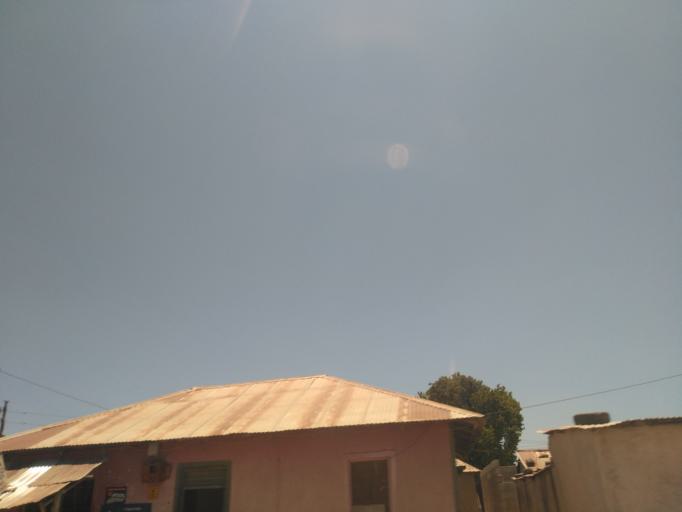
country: TZ
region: Dodoma
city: Dodoma
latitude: -6.1626
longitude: 35.7411
